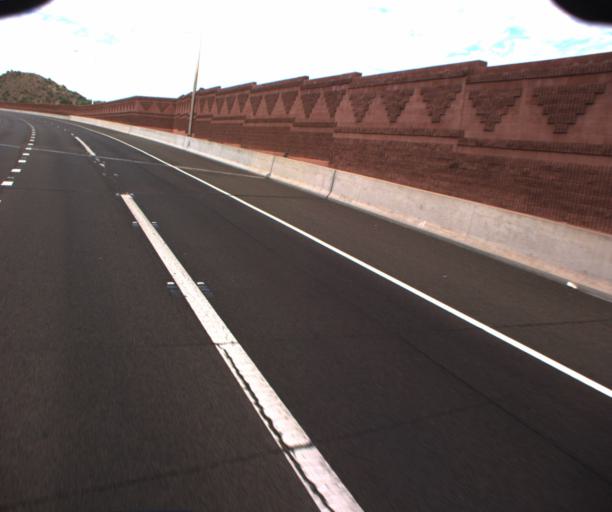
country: US
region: Arizona
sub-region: Pinal County
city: Apache Junction
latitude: 33.4274
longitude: -111.6359
